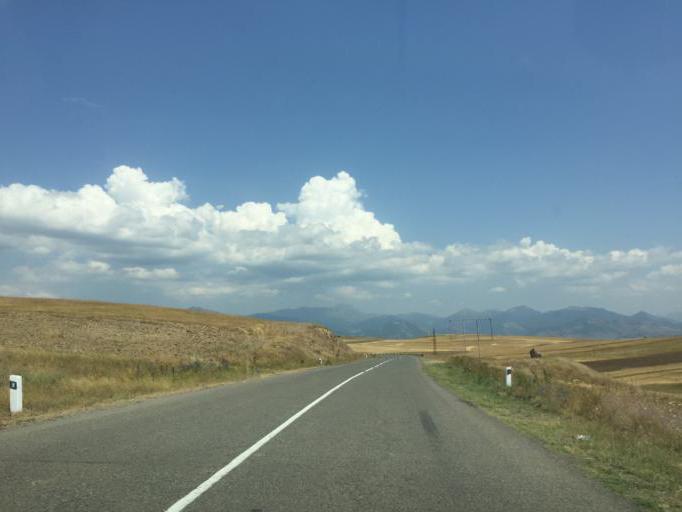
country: AM
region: Syunik'i Marz
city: Tegh
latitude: 39.5820
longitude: 46.4932
